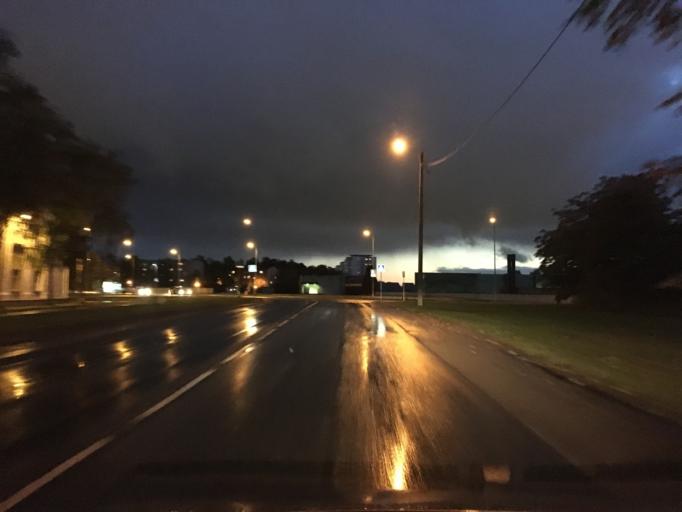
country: EE
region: Harju
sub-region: Tallinna linn
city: Tallinn
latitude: 59.4369
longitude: 24.7996
